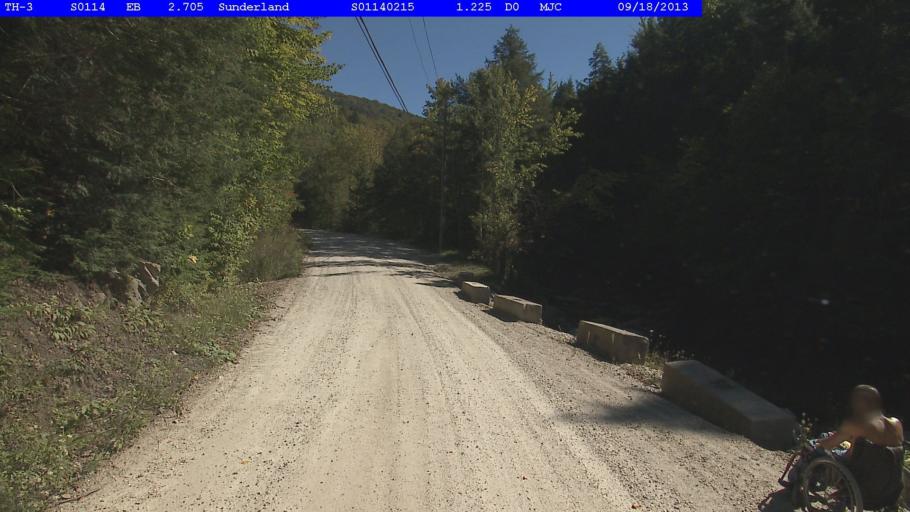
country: US
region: Vermont
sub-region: Bennington County
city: Arlington
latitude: 43.0551
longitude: -73.1173
